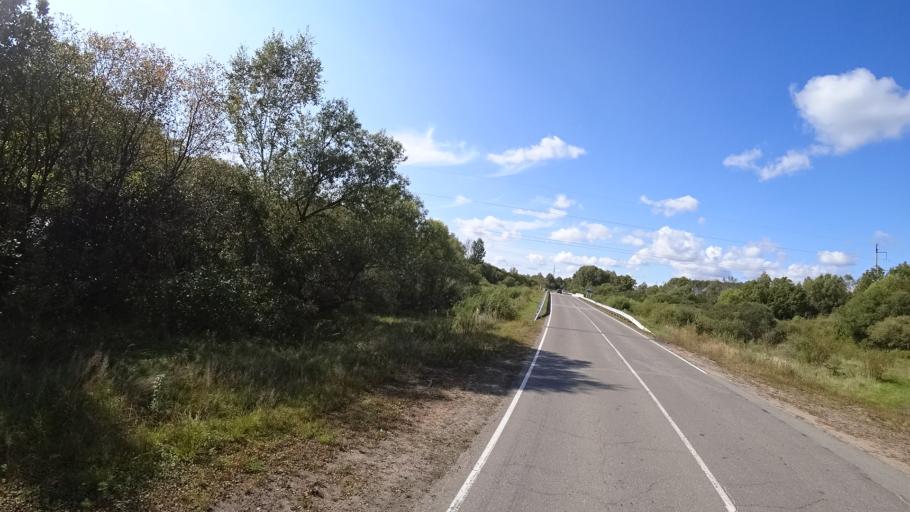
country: RU
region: Amur
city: Arkhara
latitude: 49.4059
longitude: 130.1252
